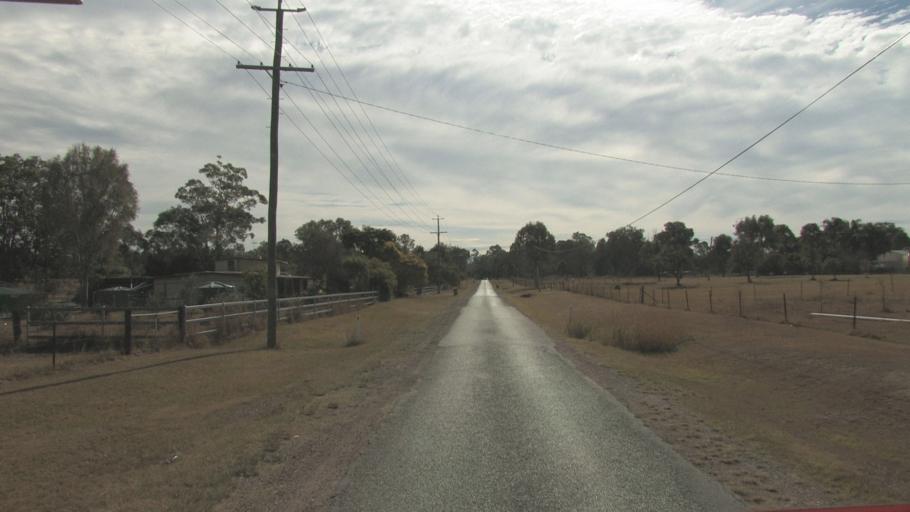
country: AU
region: Queensland
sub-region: Logan
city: North Maclean
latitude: -27.7788
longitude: 153.0079
